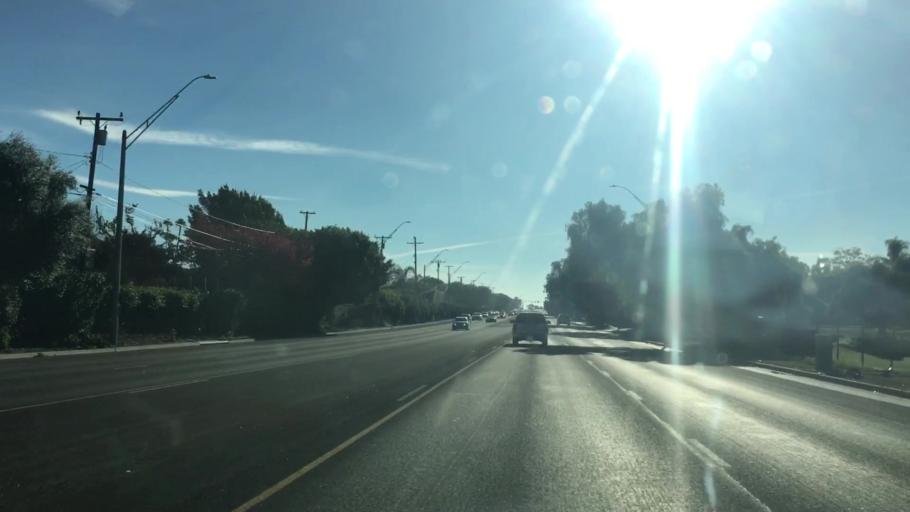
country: US
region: California
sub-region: Orange County
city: Rossmoor
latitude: 33.7801
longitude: -118.1293
